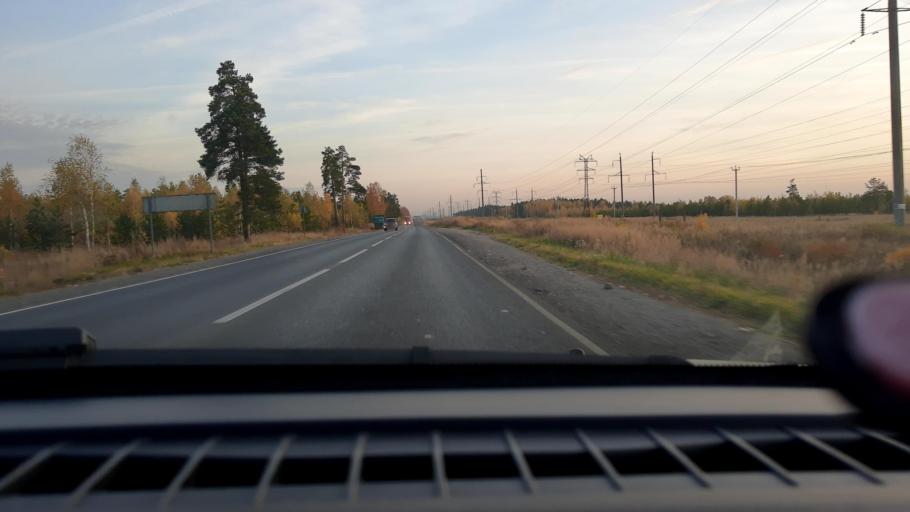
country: RU
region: Nizjnij Novgorod
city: Babino
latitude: 56.3208
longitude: 43.5590
